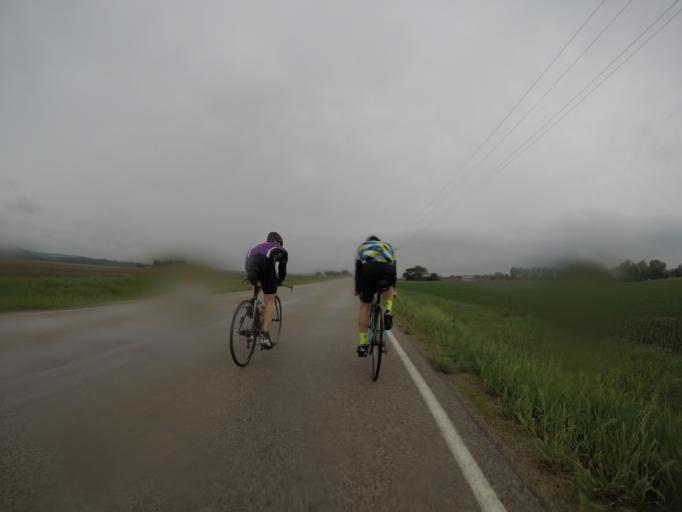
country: US
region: Kansas
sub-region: Pottawatomie County
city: Wamego
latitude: 39.3284
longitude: -96.2214
